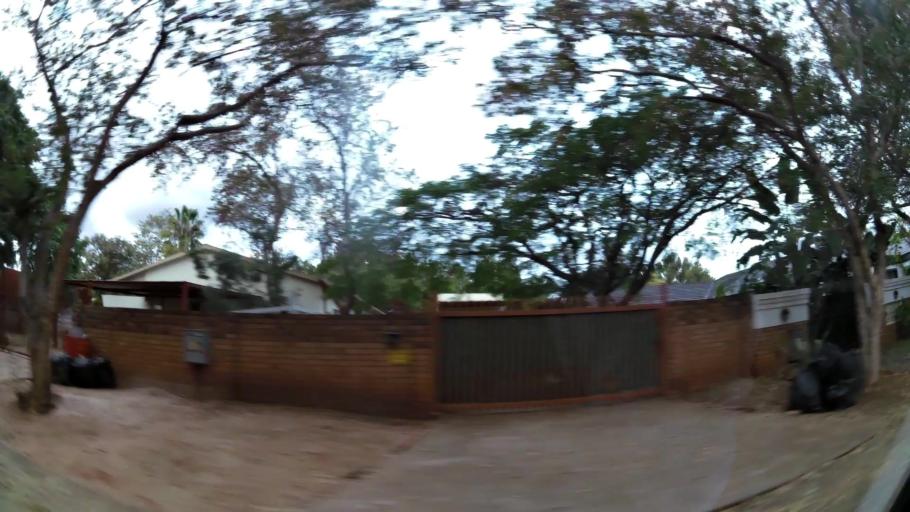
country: ZA
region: Limpopo
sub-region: Waterberg District Municipality
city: Mokopane
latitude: -24.1922
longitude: 28.9953
